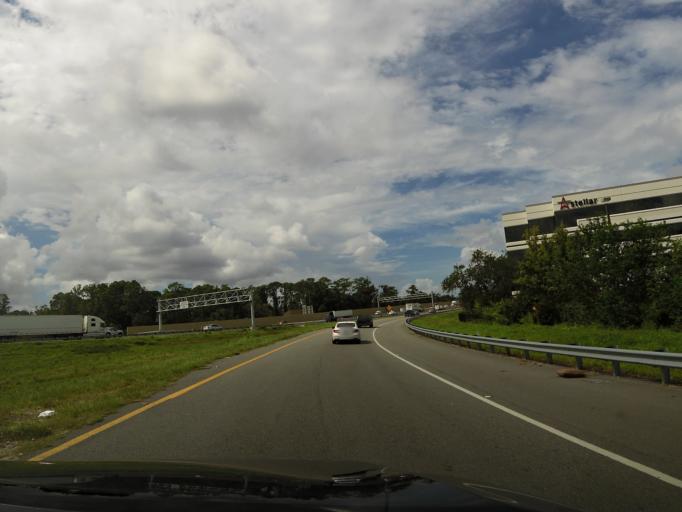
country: US
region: Florida
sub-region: Saint Johns County
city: Fruit Cove
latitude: 30.1834
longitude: -81.6306
